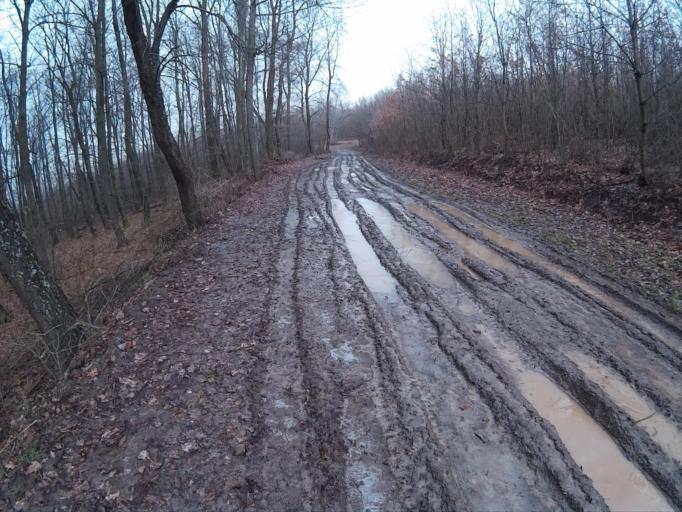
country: HU
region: Borsod-Abauj-Zemplen
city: Tolcsva
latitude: 48.3629
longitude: 21.4827
